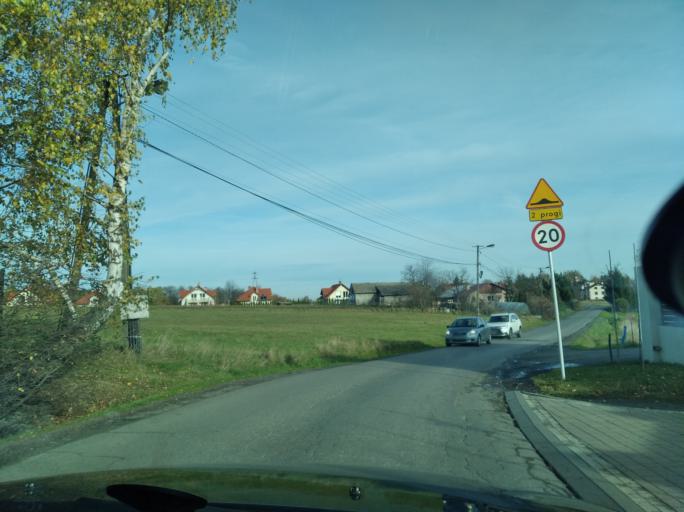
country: PL
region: Subcarpathian Voivodeship
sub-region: Powiat rzeszowski
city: Tyczyn
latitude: 49.9991
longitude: 22.0677
